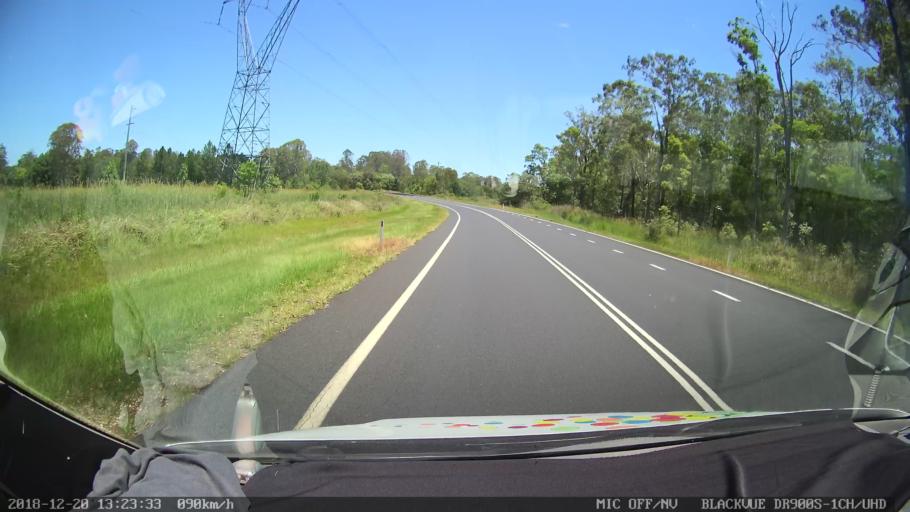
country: AU
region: New South Wales
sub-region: Richmond Valley
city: Casino
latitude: -29.1061
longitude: 152.9990
